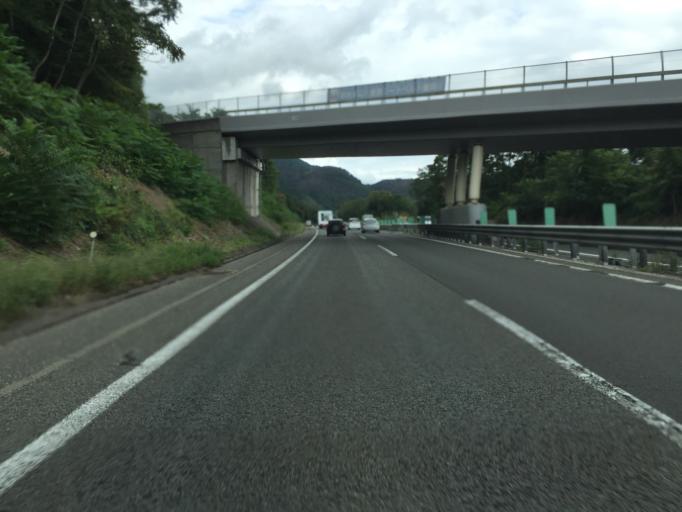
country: JP
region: Fukushima
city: Yanagawamachi-saiwaicho
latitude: 37.8862
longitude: 140.5437
